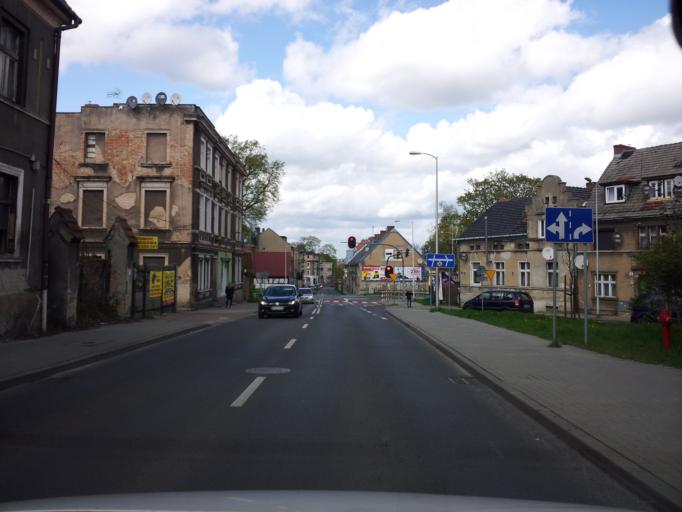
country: PL
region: Lubusz
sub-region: Zielona Gora
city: Zielona Gora
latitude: 51.9305
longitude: 15.5070
